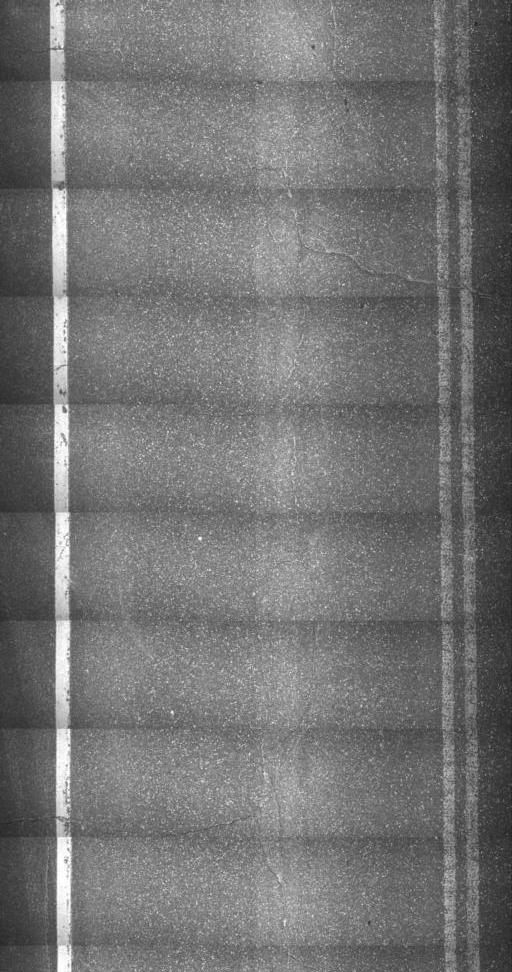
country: US
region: Vermont
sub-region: Washington County
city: Northfield
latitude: 44.0892
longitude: -72.7344
